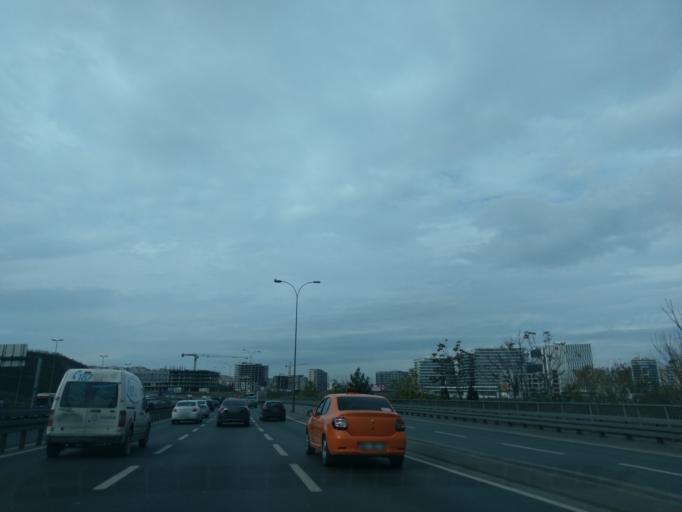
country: TR
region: Istanbul
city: Bahcelievler
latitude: 40.9964
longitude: 28.8142
